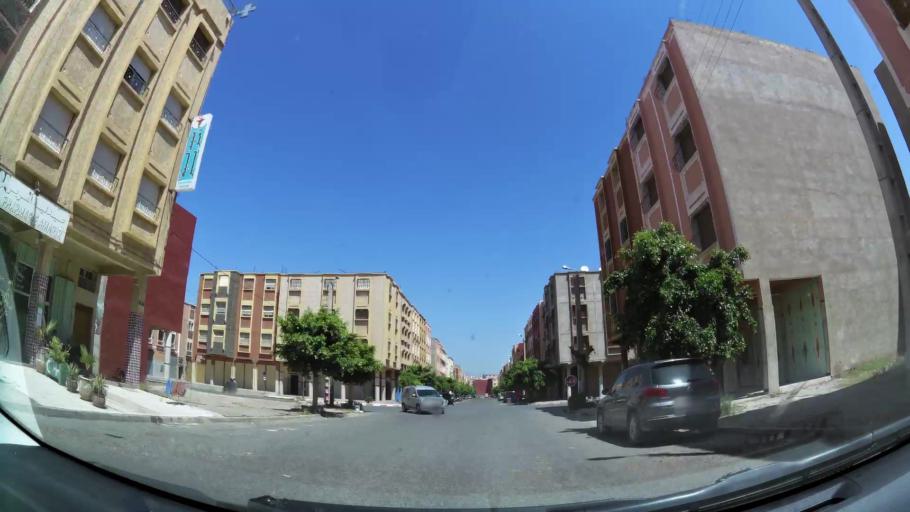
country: MA
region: Souss-Massa-Draa
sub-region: Inezgane-Ait Mellou
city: Inezgane
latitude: 30.3354
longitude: -9.5019
